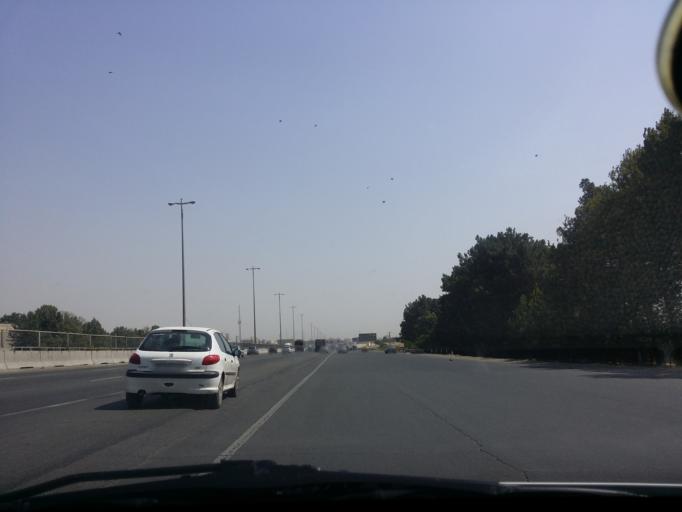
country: IR
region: Alborz
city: Karaj
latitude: 35.8443
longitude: 50.9092
